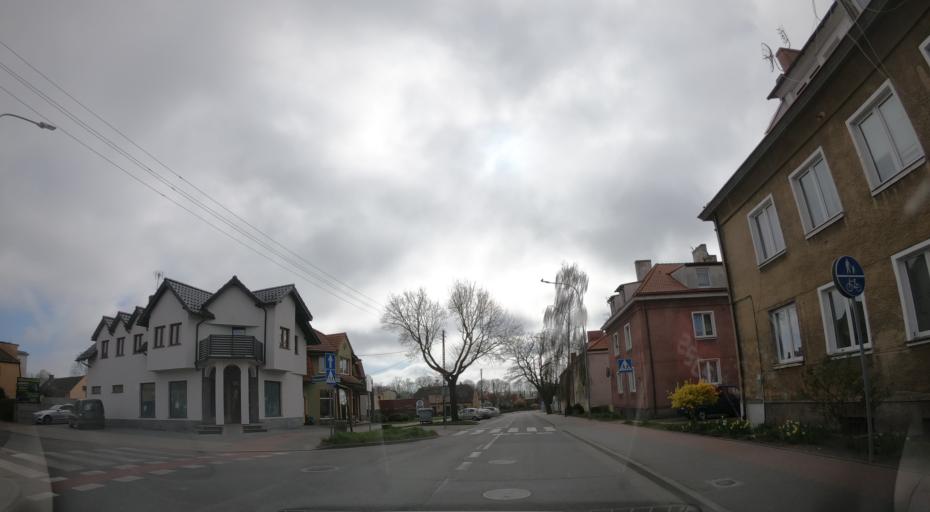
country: PL
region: West Pomeranian Voivodeship
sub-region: Powiat kamienski
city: Kamien Pomorski
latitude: 53.9666
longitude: 14.7784
